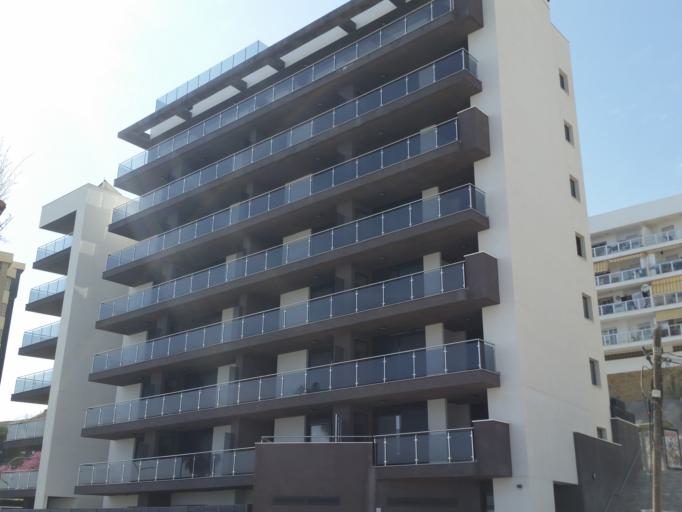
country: ES
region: Andalusia
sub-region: Provincia de Malaga
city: Benalmadena
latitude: 36.5697
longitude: -4.5931
